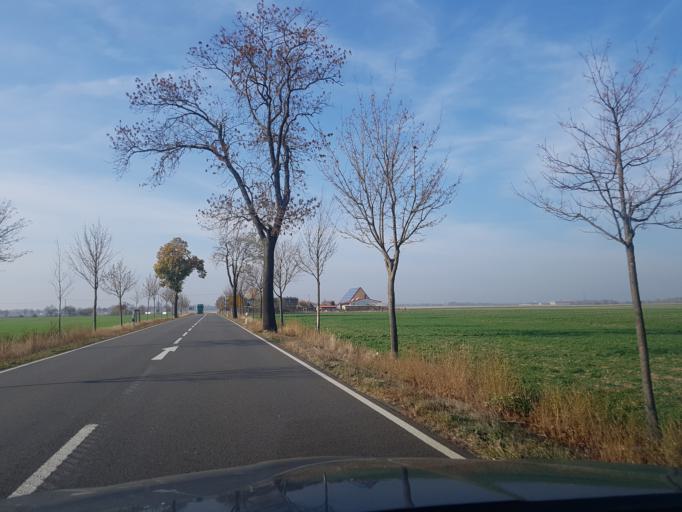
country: DE
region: Saxony
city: Beilrode
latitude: 51.5500
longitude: 13.0906
